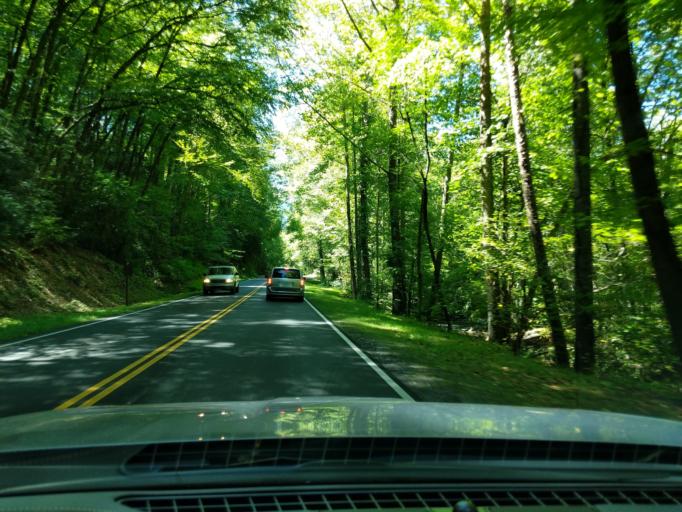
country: US
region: North Carolina
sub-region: Swain County
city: Cherokee
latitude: 35.5552
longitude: -83.3122
